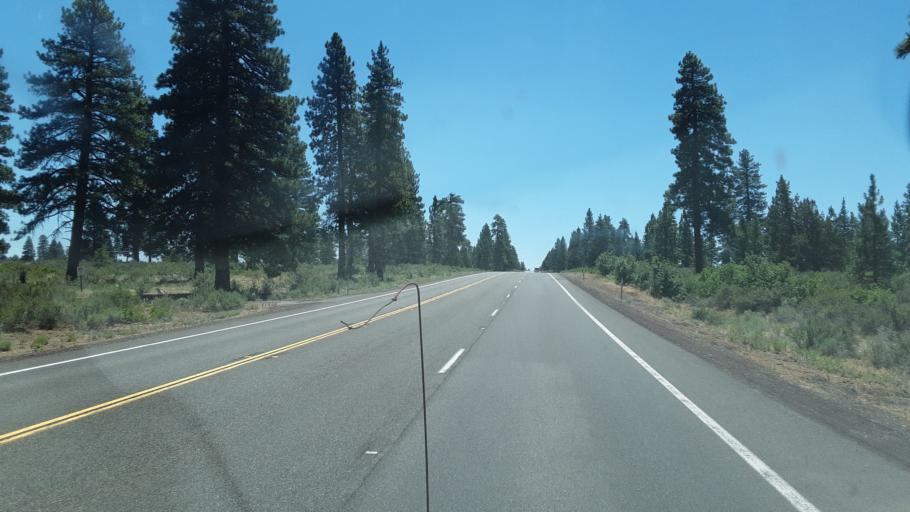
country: US
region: California
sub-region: Siskiyou County
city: Tulelake
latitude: 41.6102
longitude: -121.2117
